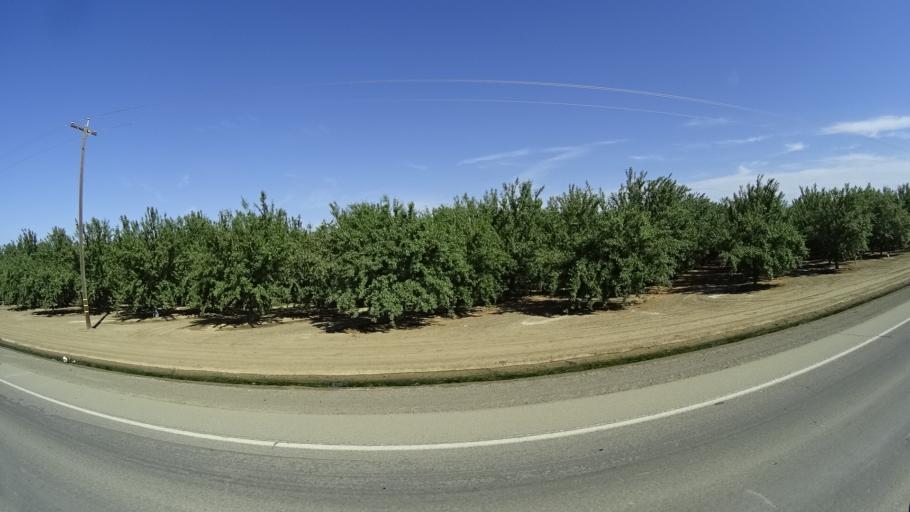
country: US
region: California
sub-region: Kings County
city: Lemoore Station
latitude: 36.1677
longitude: -119.9731
